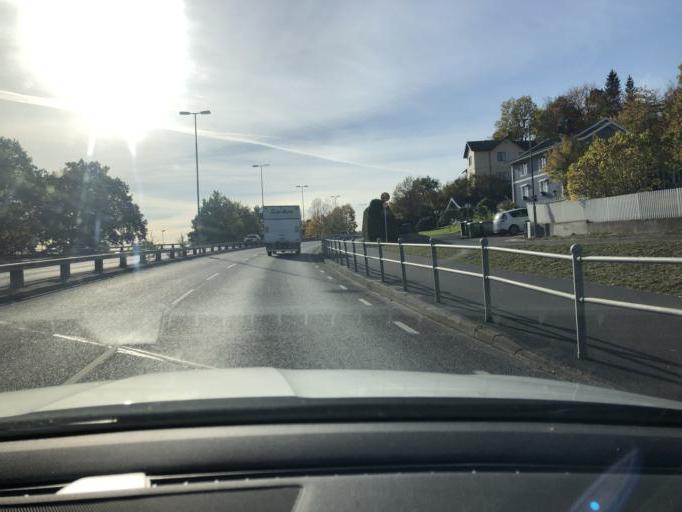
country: SE
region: Joenkoeping
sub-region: Jonkopings Kommun
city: Jonkoping
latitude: 57.7744
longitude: 14.1406
